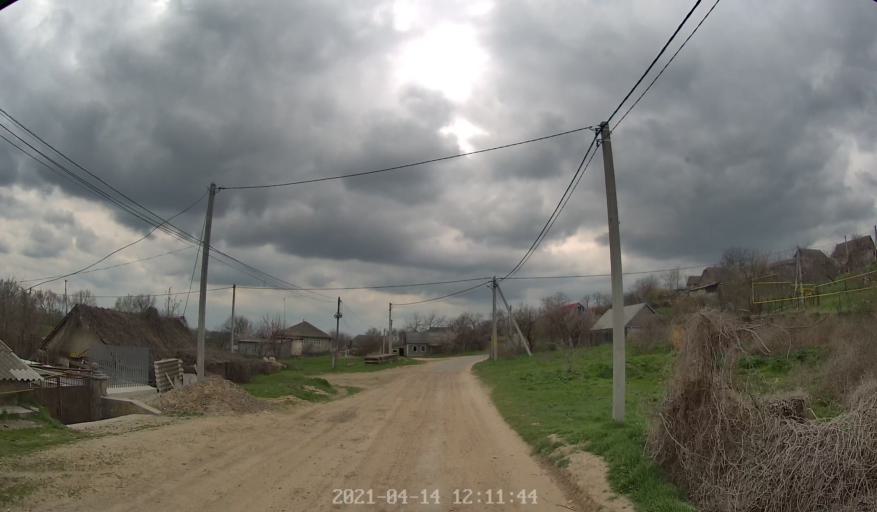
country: MD
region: Criuleni
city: Criuleni
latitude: 47.1658
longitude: 29.2023
